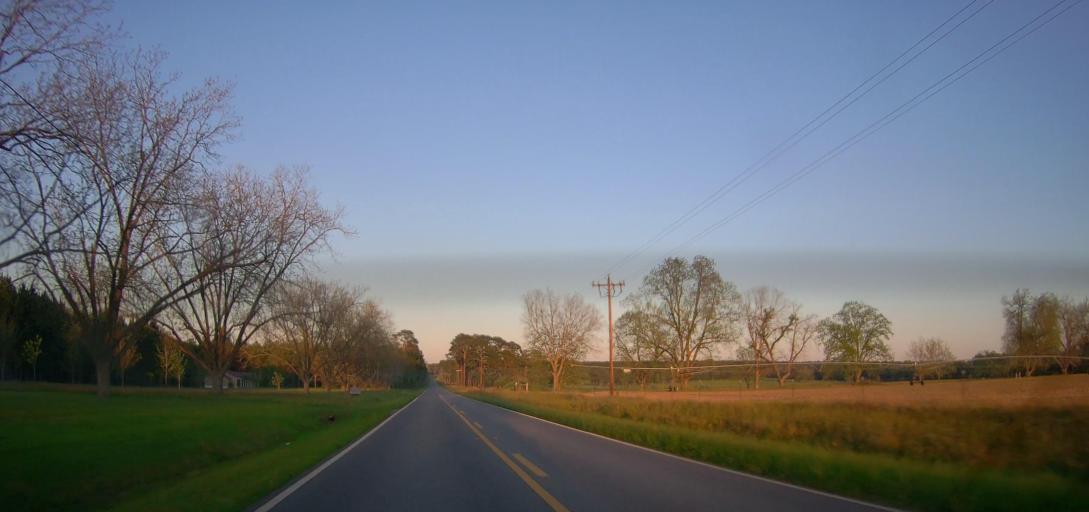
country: US
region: Georgia
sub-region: Ben Hill County
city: Fitzgerald
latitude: 31.7180
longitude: -83.3041
